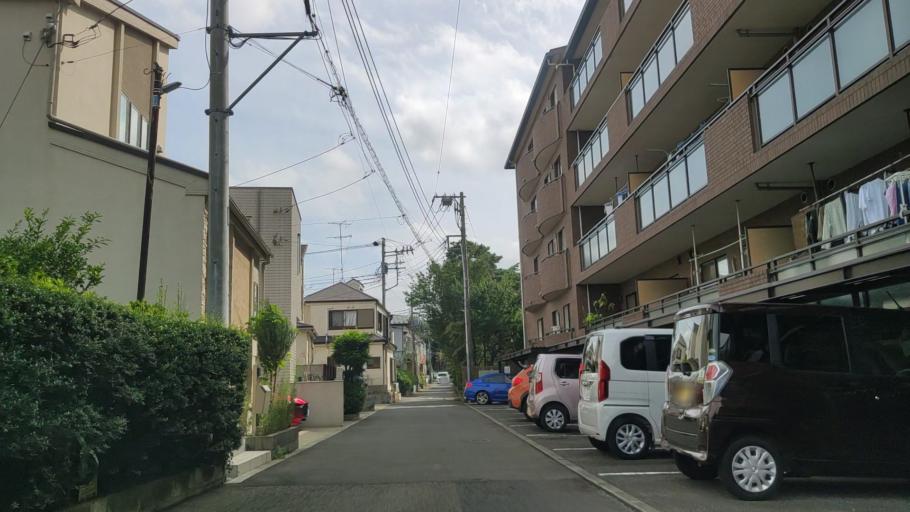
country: JP
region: Kanagawa
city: Minami-rinkan
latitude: 35.5112
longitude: 139.4405
